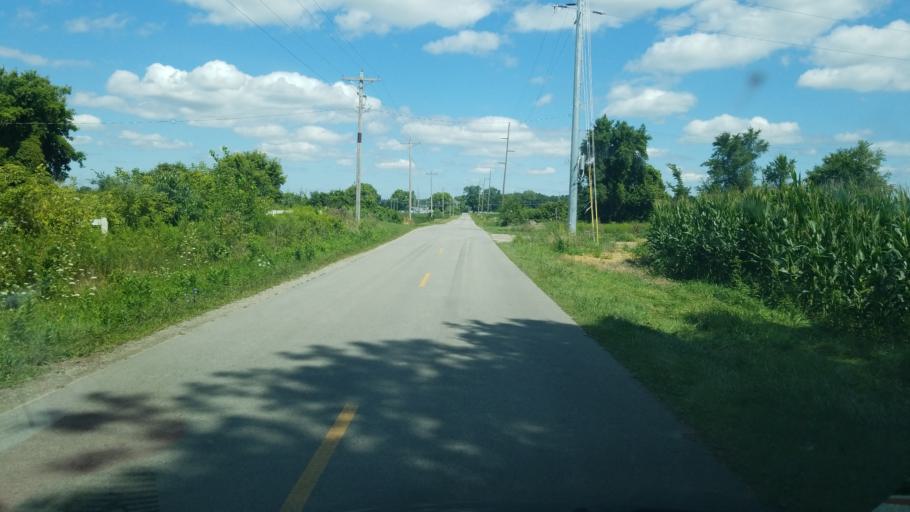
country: US
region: Ohio
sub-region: Henry County
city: Liberty Center
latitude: 41.4679
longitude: -83.9413
